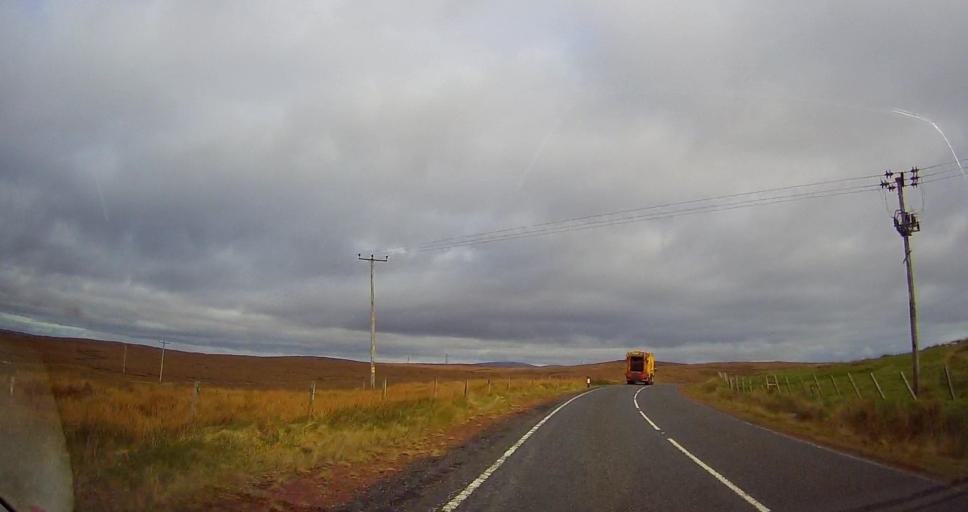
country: GB
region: Scotland
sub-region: Shetland Islands
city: Lerwick
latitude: 60.4475
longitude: -1.2093
